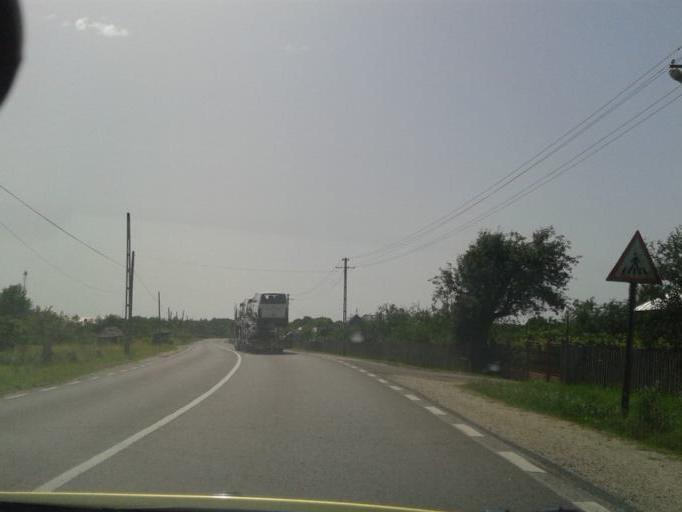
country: RO
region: Arges
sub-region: Comuna Cotmeana
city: Cotmeana
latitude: 44.9843
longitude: 24.6486
